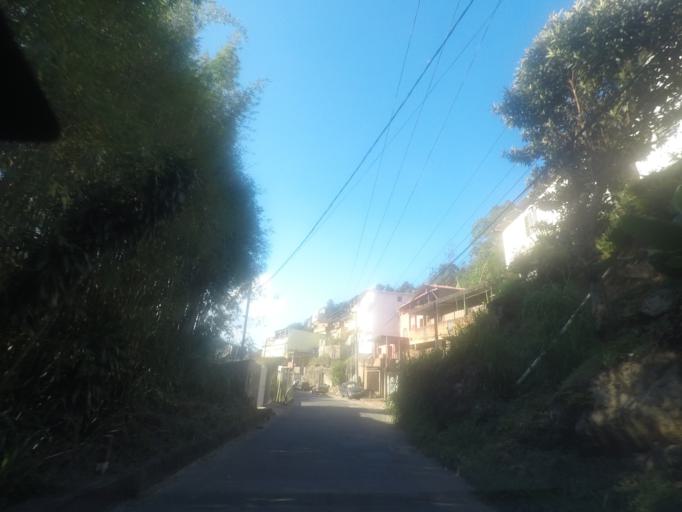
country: BR
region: Rio de Janeiro
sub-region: Petropolis
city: Petropolis
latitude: -22.4930
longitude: -43.1498
